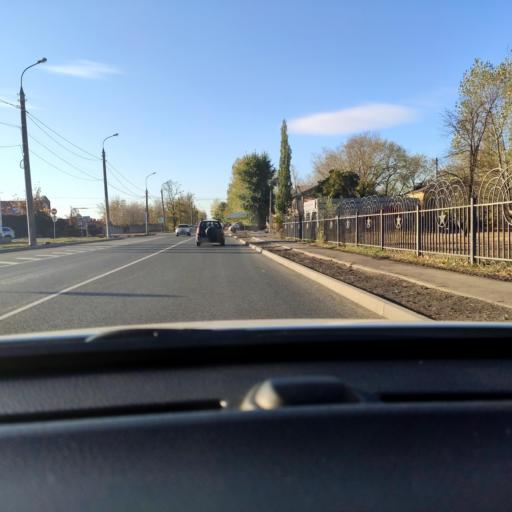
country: RU
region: Voronezj
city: Voronezh
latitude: 51.6578
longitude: 39.2489
